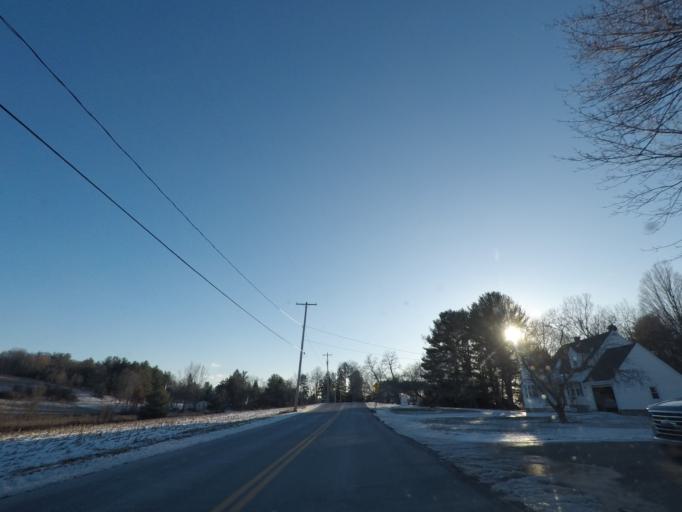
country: US
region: New York
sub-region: Rensselaer County
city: Poestenkill
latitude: 42.7236
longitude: -73.5977
